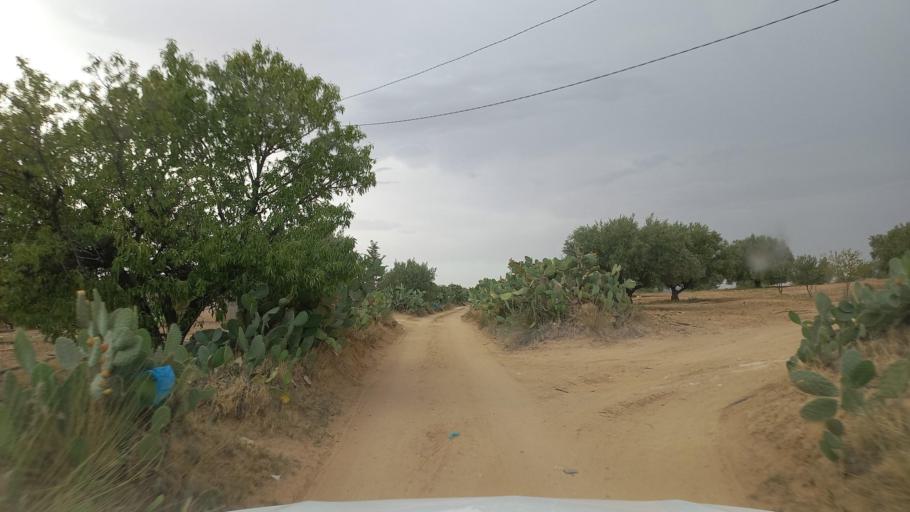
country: TN
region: Al Qasrayn
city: Kasserine
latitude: 35.2403
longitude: 9.0250
